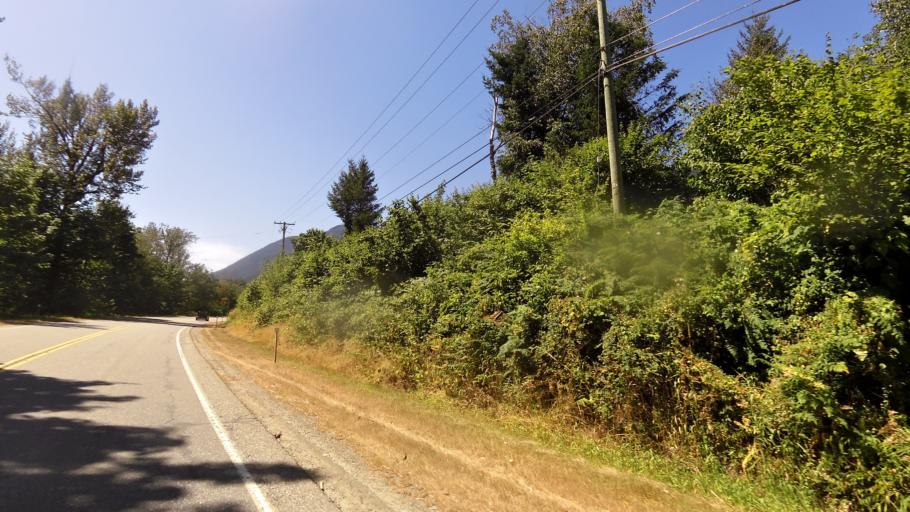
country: CA
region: British Columbia
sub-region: Fraser Valley Regional District
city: Chilliwack
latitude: 49.2031
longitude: -122.0293
